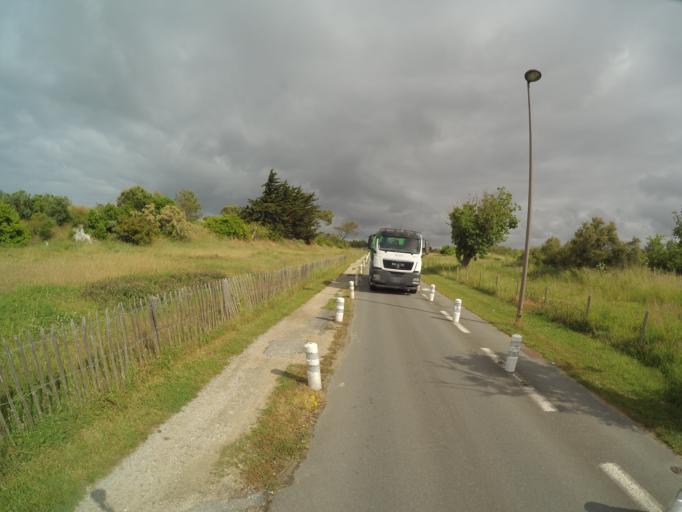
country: FR
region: Poitou-Charentes
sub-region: Departement de la Charente-Maritime
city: Aytre
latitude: 46.1219
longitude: -1.1244
